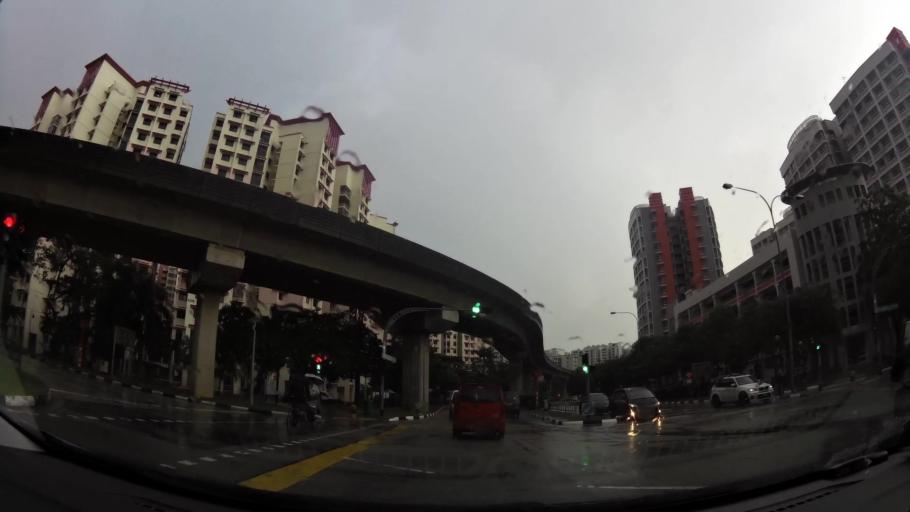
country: MY
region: Johor
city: Kampung Pasir Gudang Baru
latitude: 1.3868
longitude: 103.8939
